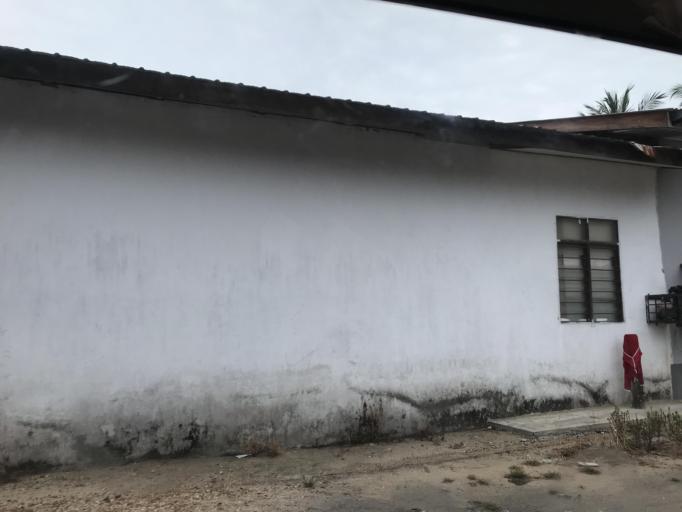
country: MY
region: Kelantan
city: Kota Bharu
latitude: 6.1666
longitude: 102.2081
